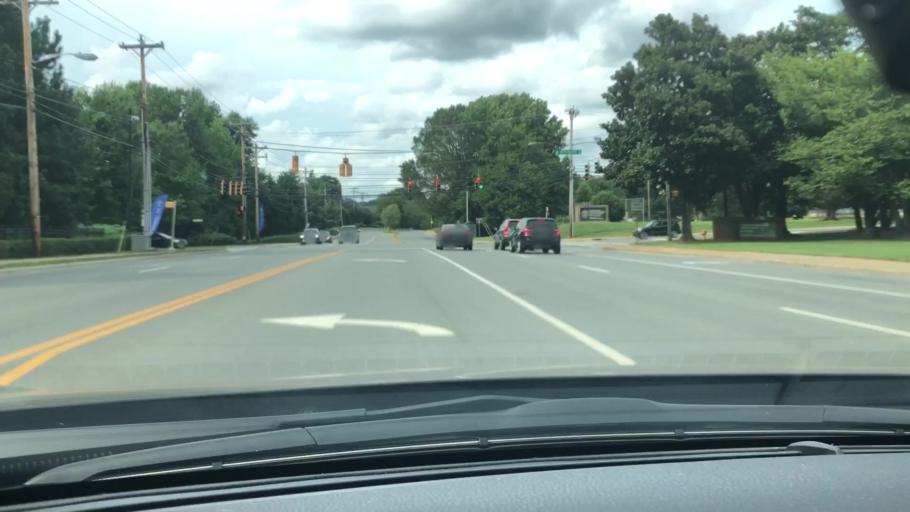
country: US
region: North Carolina
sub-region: Mecklenburg County
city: Charlotte
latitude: 35.1900
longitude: -80.8108
